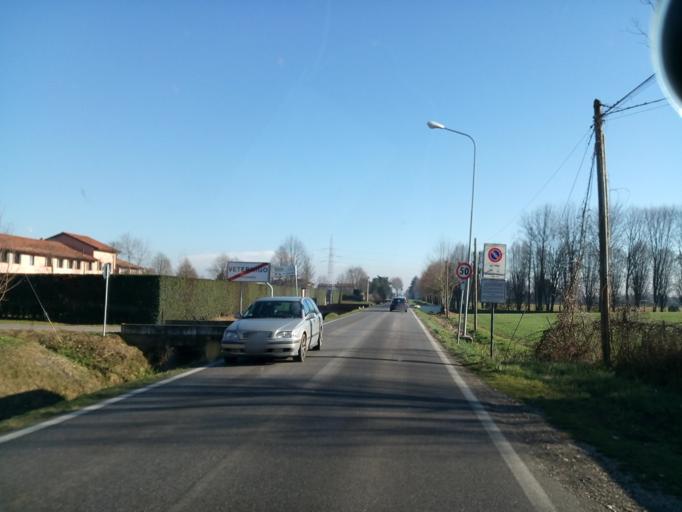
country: IT
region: Veneto
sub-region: Provincia di Venezia
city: Veternigo
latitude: 45.5123
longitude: 12.0654
